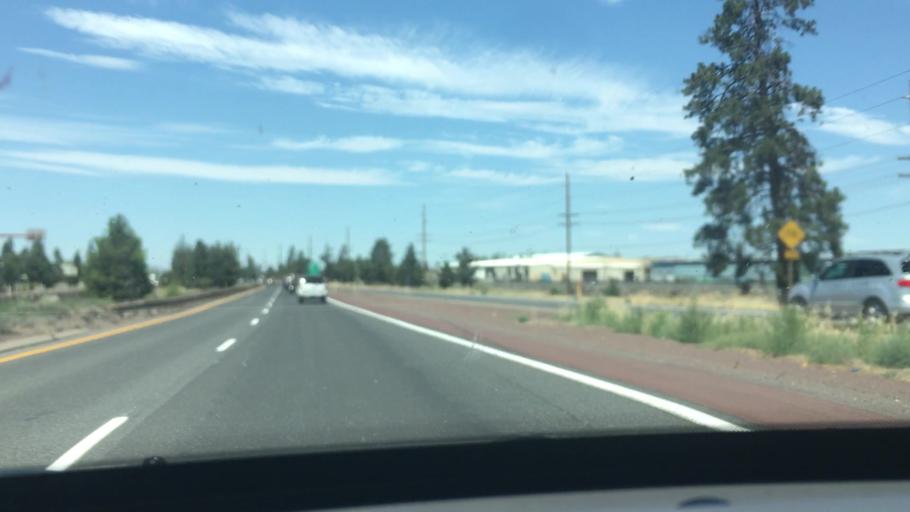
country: US
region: Oregon
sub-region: Deschutes County
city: Bend
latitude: 44.0807
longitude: -121.3012
